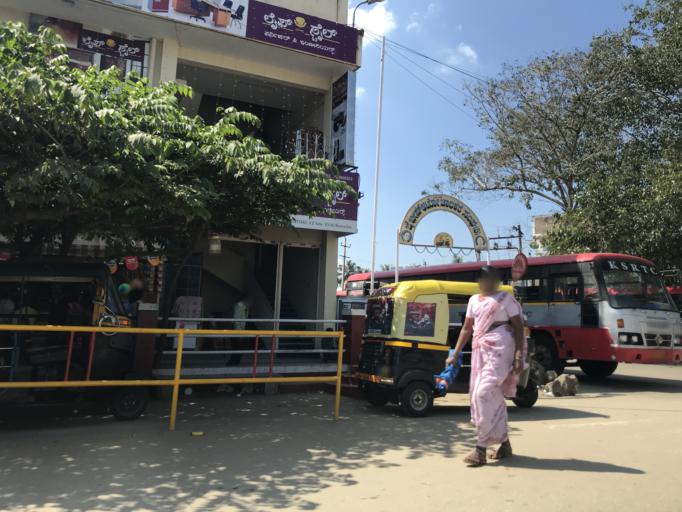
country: IN
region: Karnataka
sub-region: Mysore
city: Heggadadevankote
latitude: 12.0864
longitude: 76.3321
